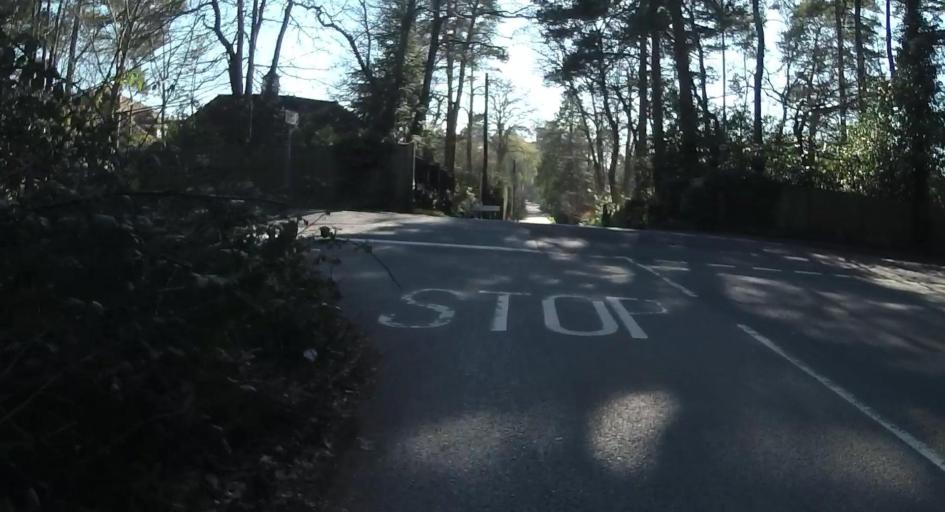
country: GB
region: England
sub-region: Royal Borough of Windsor and Maidenhead
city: Ascot
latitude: 51.3970
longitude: -0.6641
